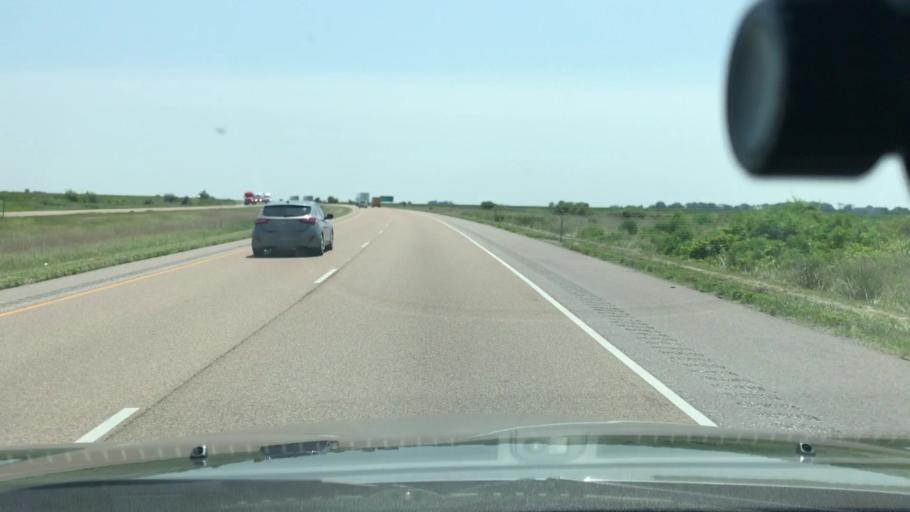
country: US
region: Illinois
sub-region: Washington County
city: Okawville
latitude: 38.4335
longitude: -89.5187
